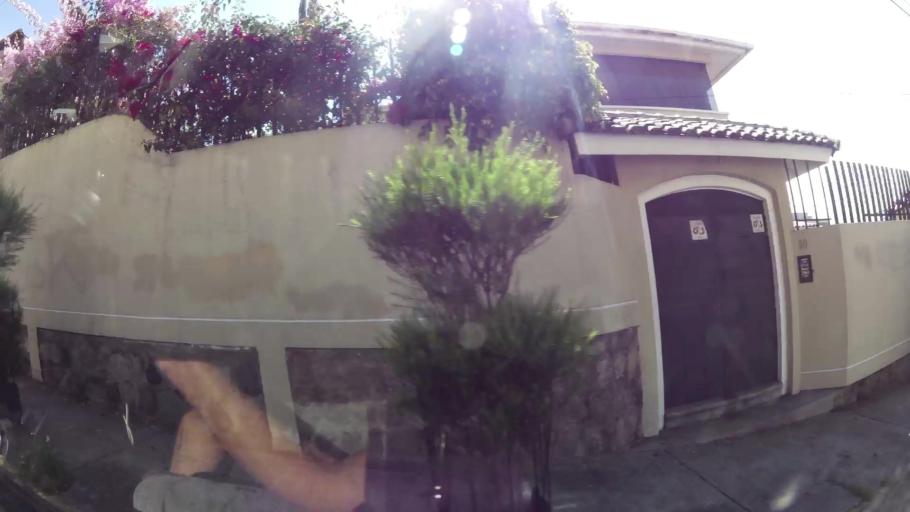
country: EC
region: Pichincha
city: Quito
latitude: -0.1986
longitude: -78.4350
